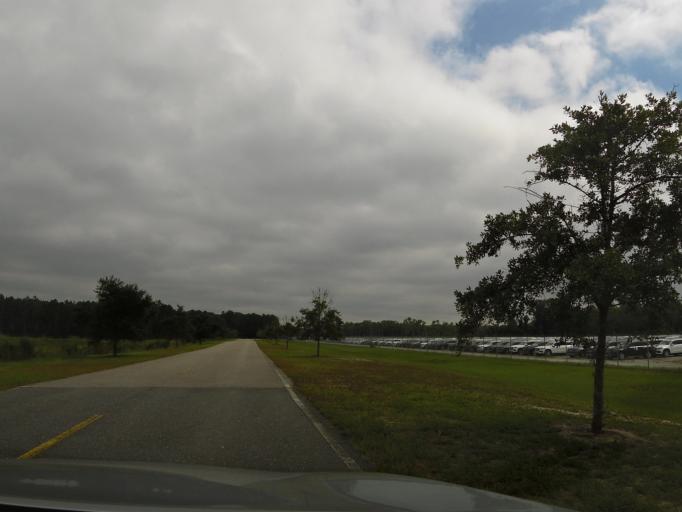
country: US
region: Georgia
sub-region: Glynn County
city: Brunswick
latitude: 31.1078
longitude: -81.5389
